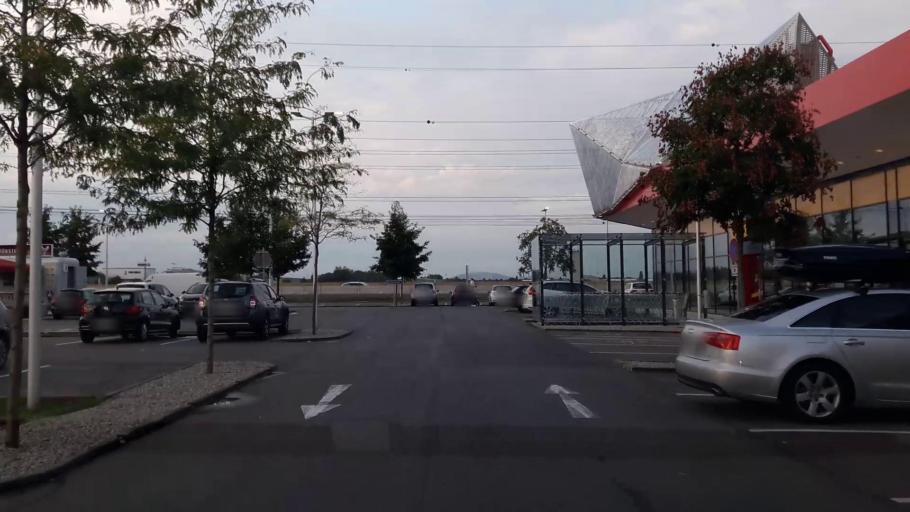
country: AT
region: Burgenland
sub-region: Politischer Bezirk Neusiedl am See
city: Parndorf
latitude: 47.9755
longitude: 16.8551
